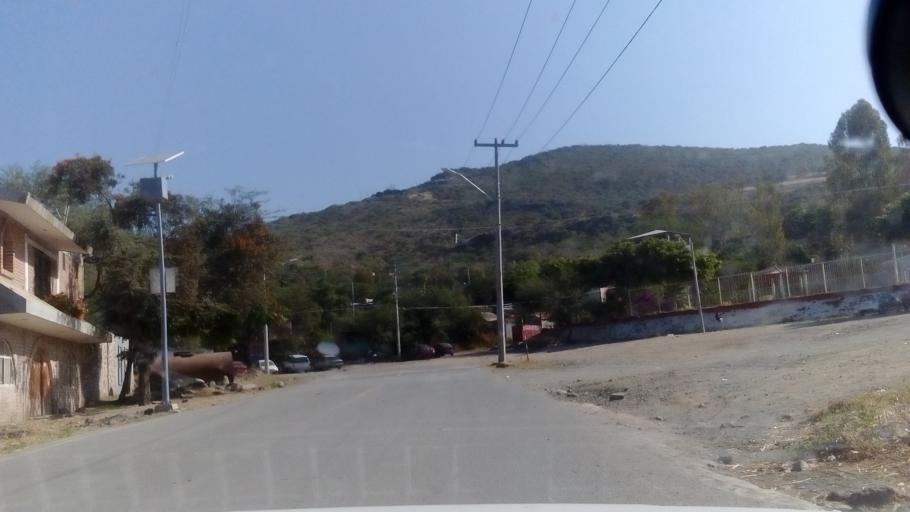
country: MX
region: Guanajuato
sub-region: Leon
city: Medina
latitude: 21.1468
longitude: -101.6080
